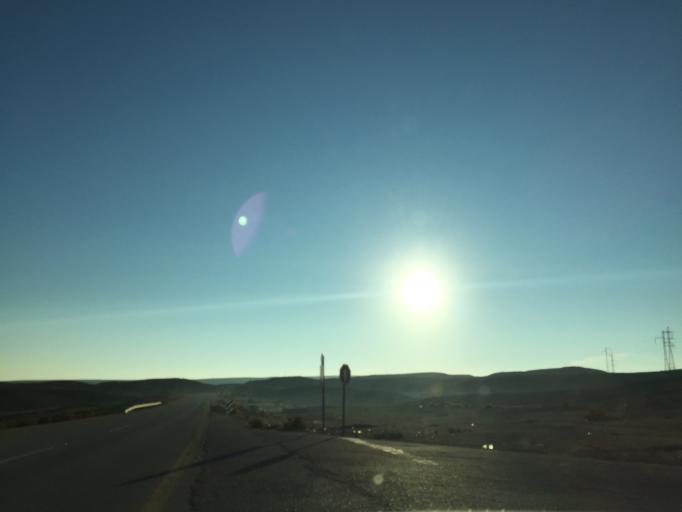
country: IL
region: Southern District
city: Mitzpe Ramon
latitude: 30.5306
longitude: 34.9207
